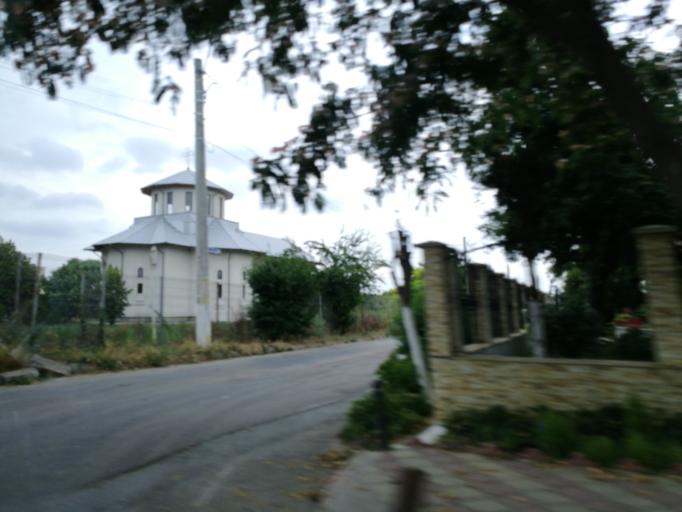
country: RO
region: Constanta
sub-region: Municipiul Mangalia
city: Mangalia
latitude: 43.8168
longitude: 28.5735
